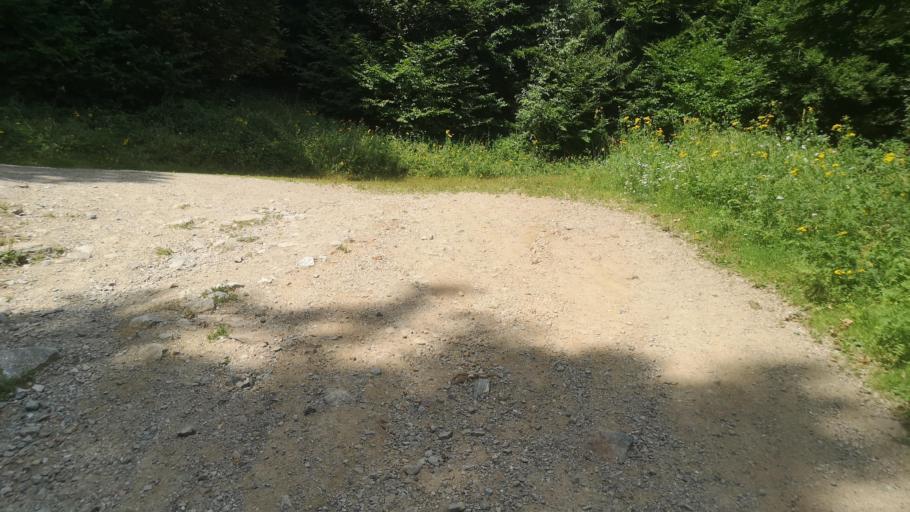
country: SK
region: Zilinsky
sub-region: Okres Zilina
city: Vrutky
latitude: 49.0878
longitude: 18.8653
